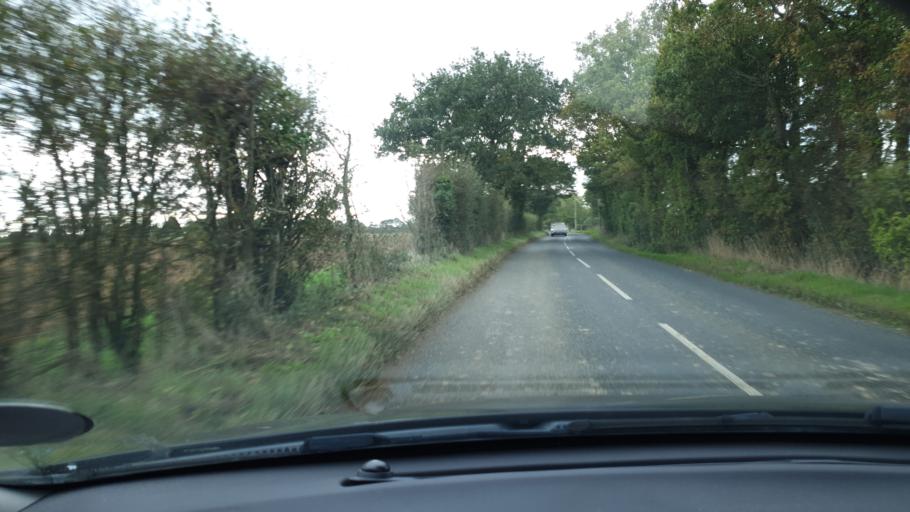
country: GB
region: England
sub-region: Essex
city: Manningtree
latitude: 51.9249
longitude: 1.0482
